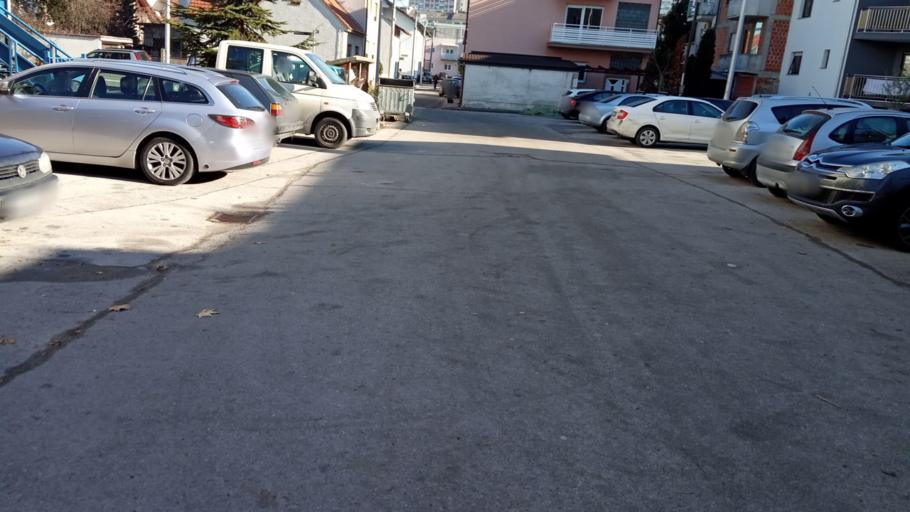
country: HR
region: Grad Zagreb
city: Jankomir
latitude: 45.7905
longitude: 15.9322
